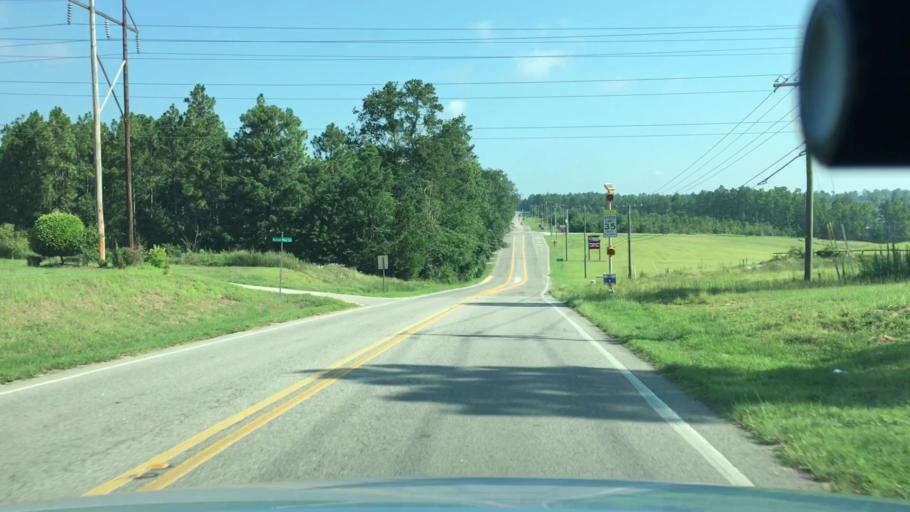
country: US
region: South Carolina
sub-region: Aiken County
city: Graniteville
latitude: 33.5808
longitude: -81.8360
